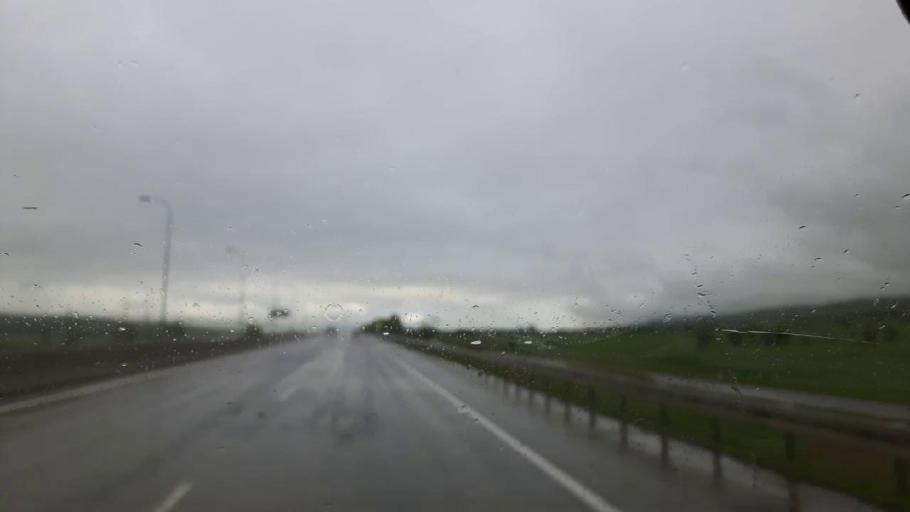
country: GE
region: Shida Kartli
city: Kaspi
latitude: 42.0191
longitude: 44.3115
